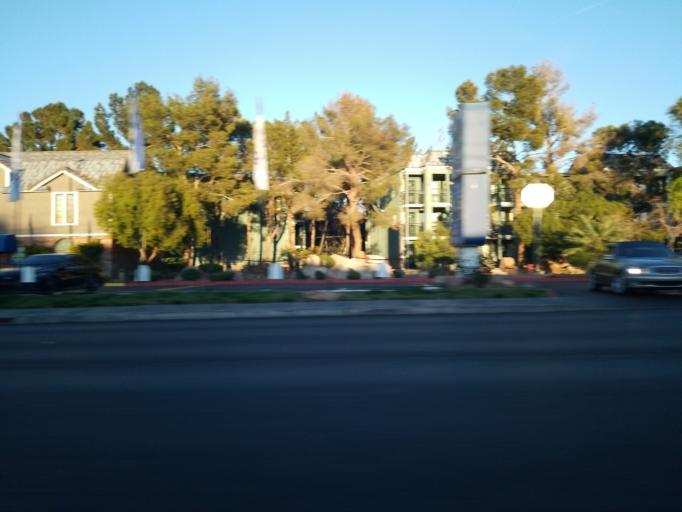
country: US
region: Nevada
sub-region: Clark County
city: Paradise
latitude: 36.1207
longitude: -115.1462
